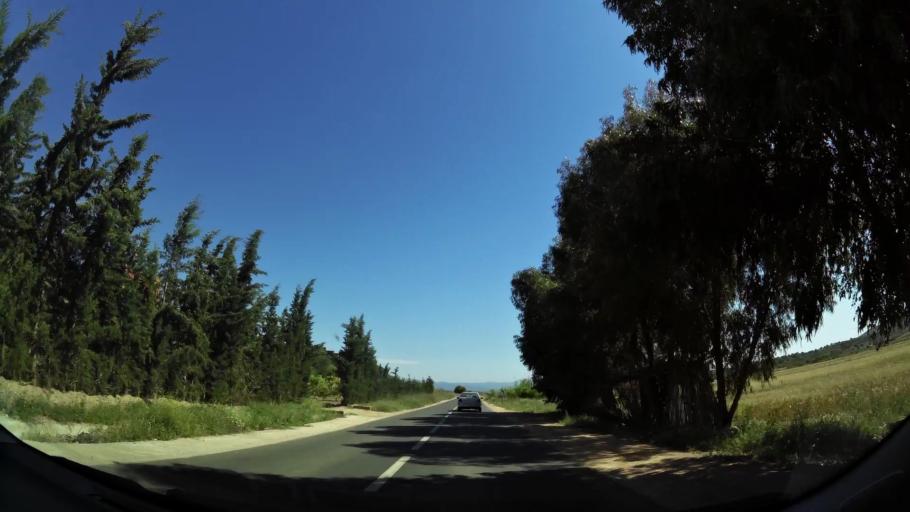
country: MA
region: Oriental
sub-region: Berkane-Taourirt
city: Madagh
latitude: 35.0464
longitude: -2.4291
